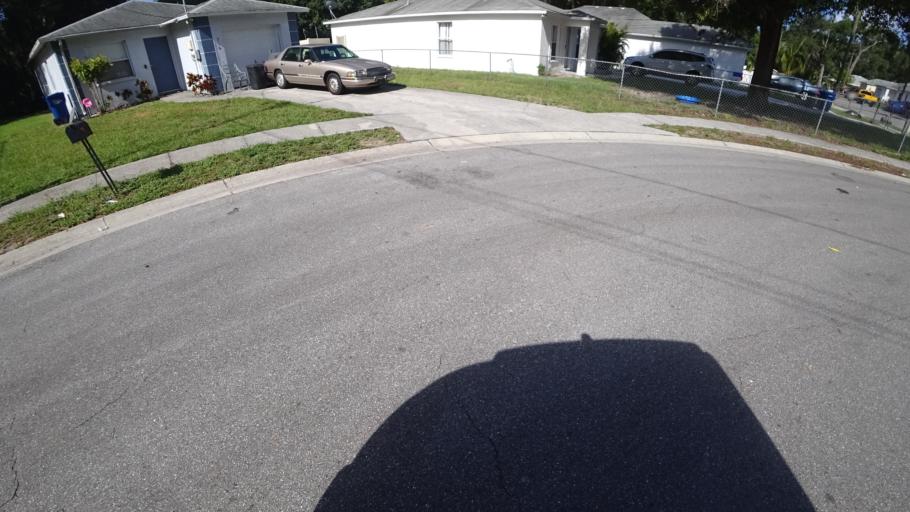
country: US
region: Florida
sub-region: Manatee County
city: West Samoset
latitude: 27.4747
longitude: -82.5673
